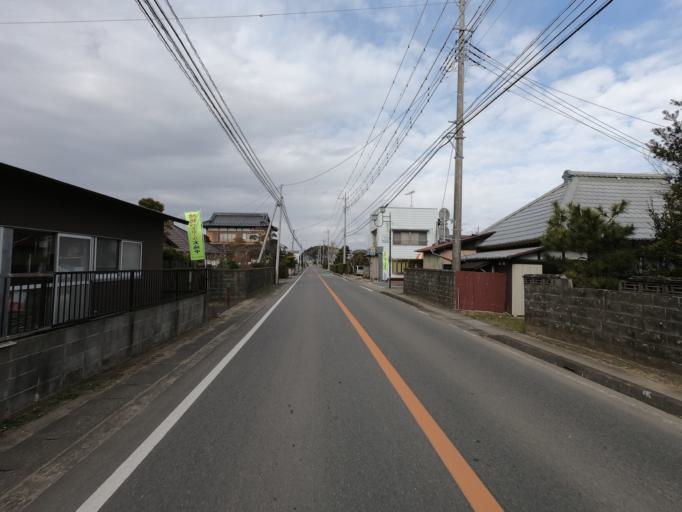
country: JP
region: Ibaraki
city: Inashiki
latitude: 36.0871
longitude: 140.4247
